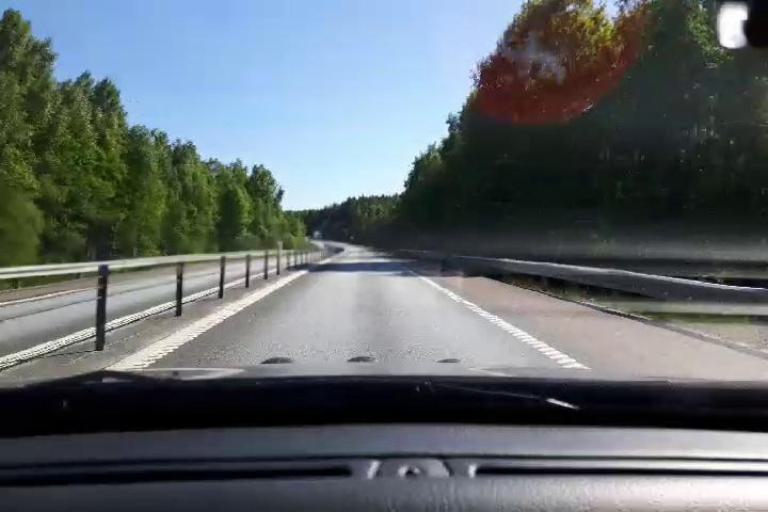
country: SE
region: Gaevleborg
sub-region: Soderhamns Kommun
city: Soderhamn
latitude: 61.2755
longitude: 17.0267
